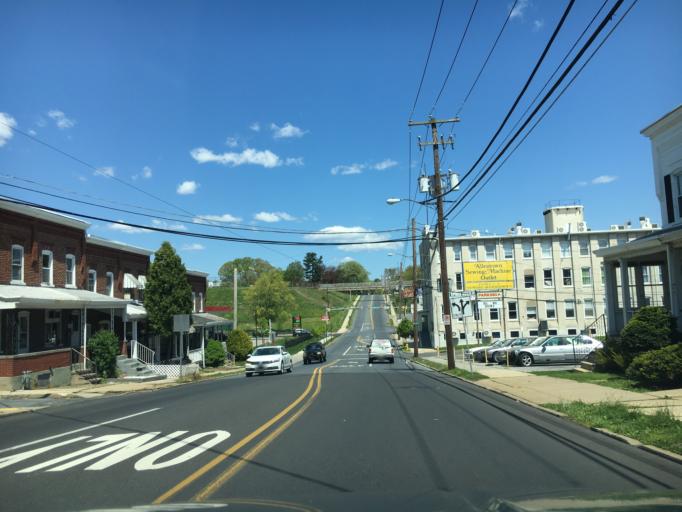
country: US
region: Pennsylvania
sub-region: Lehigh County
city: Allentown
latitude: 40.6076
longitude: -75.4927
